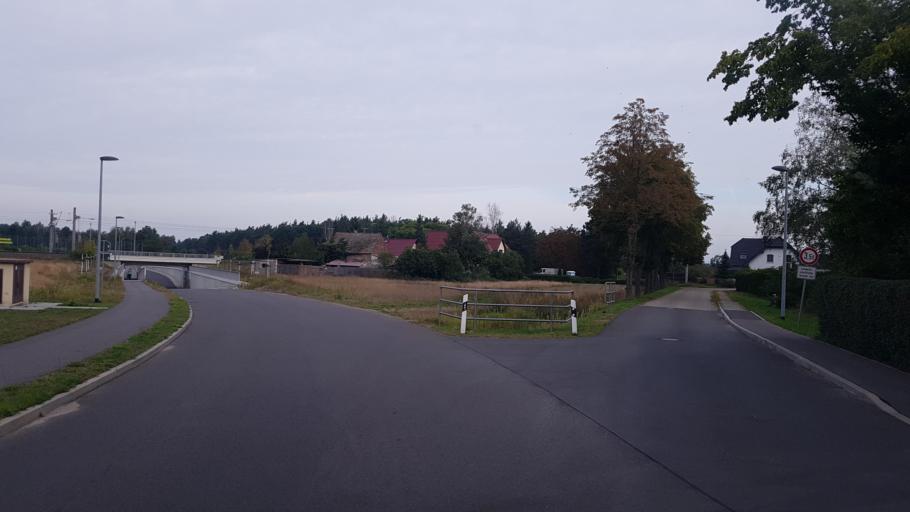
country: DE
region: Brandenburg
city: Sonnewalde
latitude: 51.7780
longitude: 13.6212
